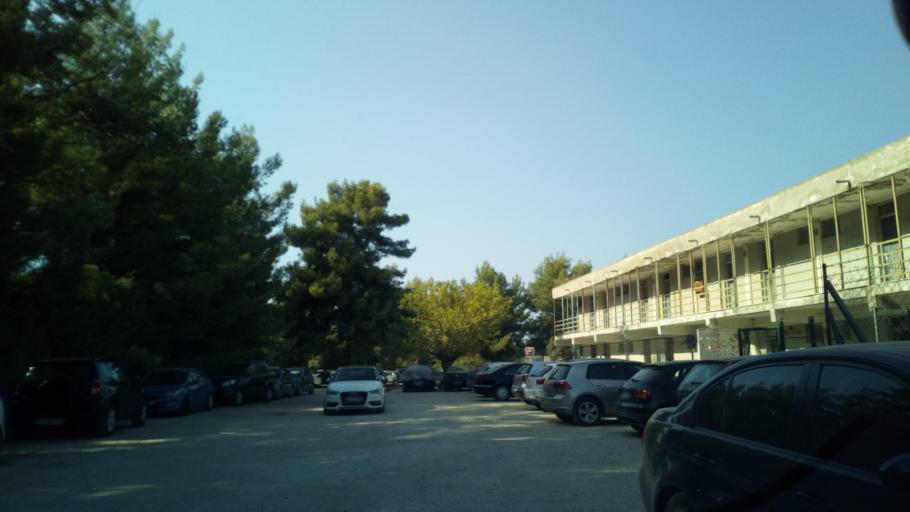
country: GR
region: Central Macedonia
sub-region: Nomos Chalkidikis
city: Pefkochori
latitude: 39.9608
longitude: 23.6755
